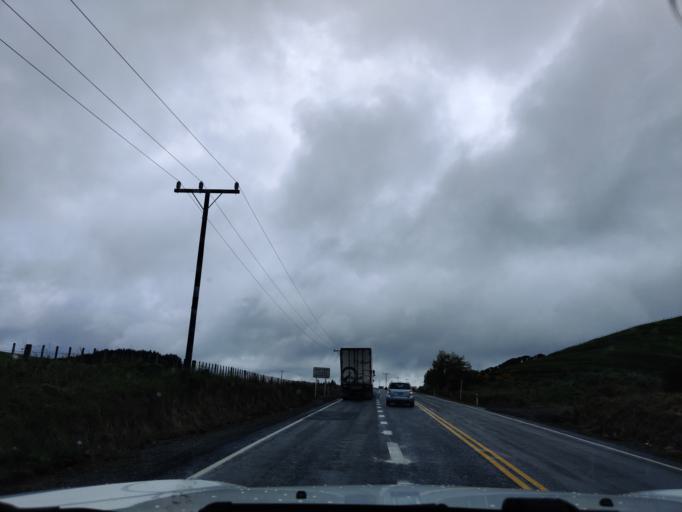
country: NZ
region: Manawatu-Wanganui
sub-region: Ruapehu District
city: Waiouru
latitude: -39.5405
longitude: 175.6819
